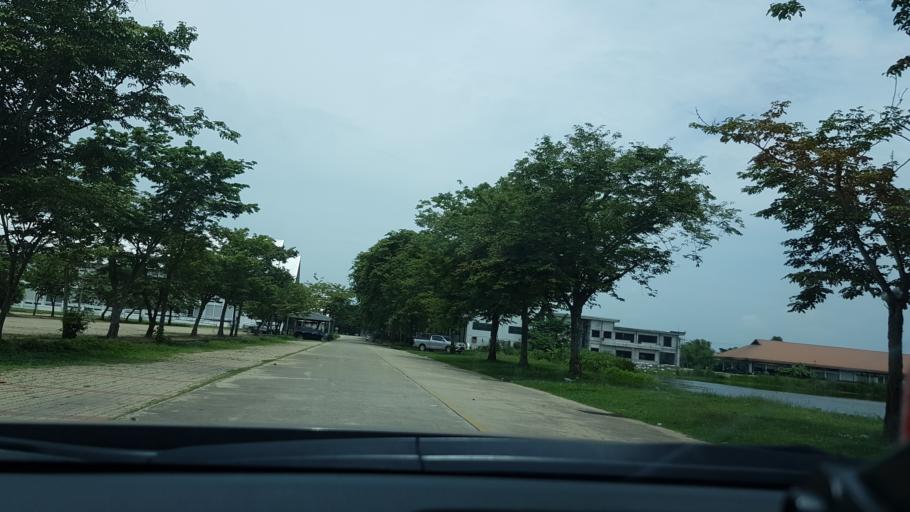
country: TH
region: Pathum Thani
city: Sam Khok
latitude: 14.1491
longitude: 100.5213
